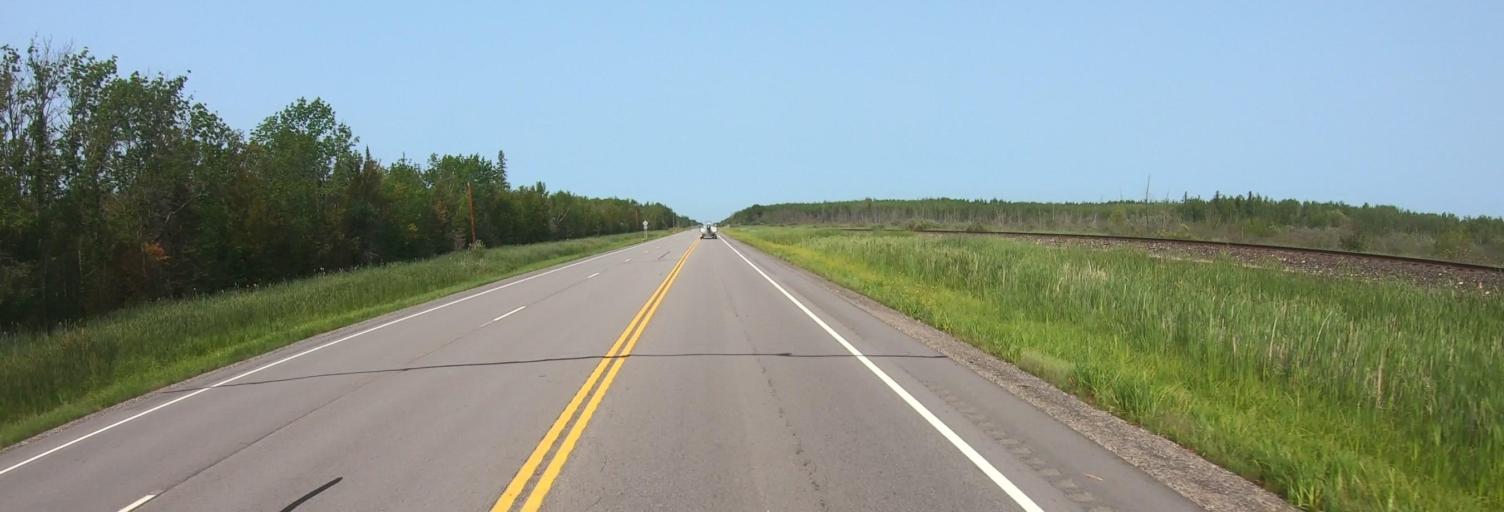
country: CA
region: Ontario
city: Fort Frances
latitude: 48.4376
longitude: -93.2510
